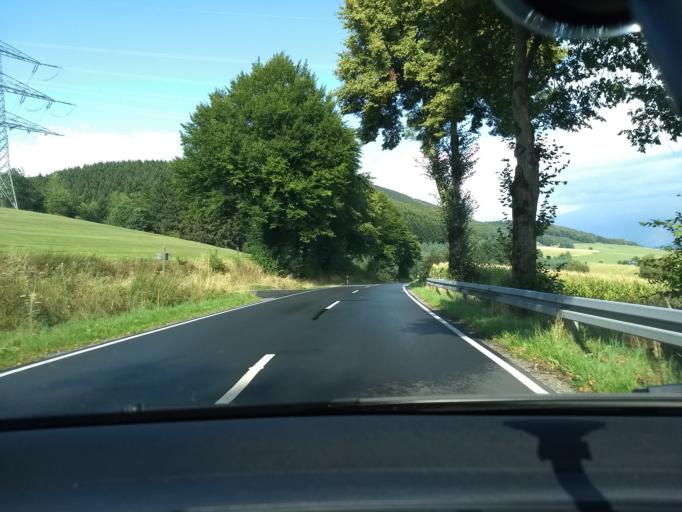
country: DE
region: North Rhine-Westphalia
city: Eslohe
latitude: 51.2476
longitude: 8.0871
